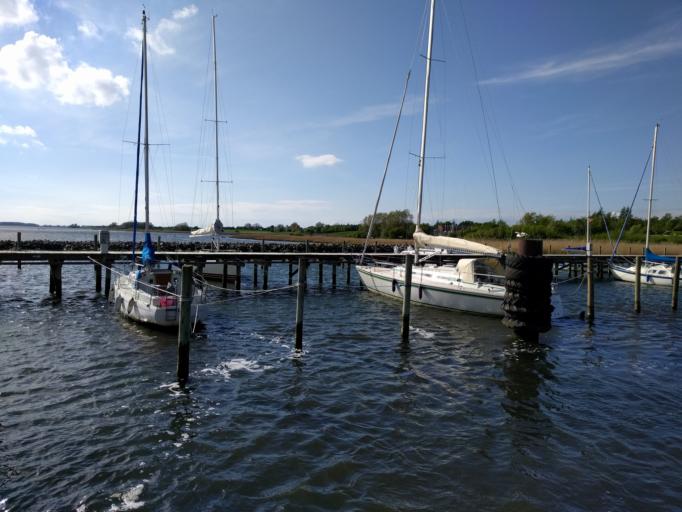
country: DK
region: Zealand
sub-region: Guldborgsund Kommune
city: Stubbekobing
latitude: 54.9125
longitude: 12.0510
